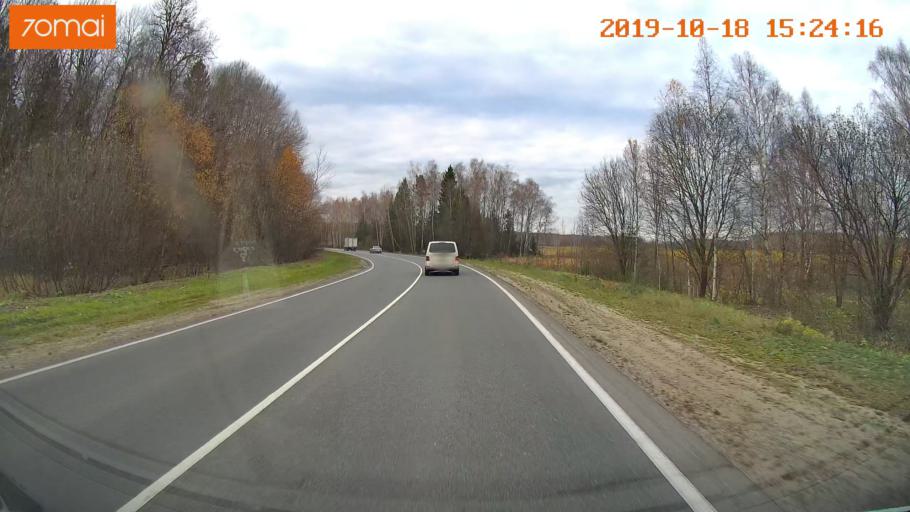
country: RU
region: Vladimir
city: Anopino
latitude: 55.7323
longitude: 40.7246
